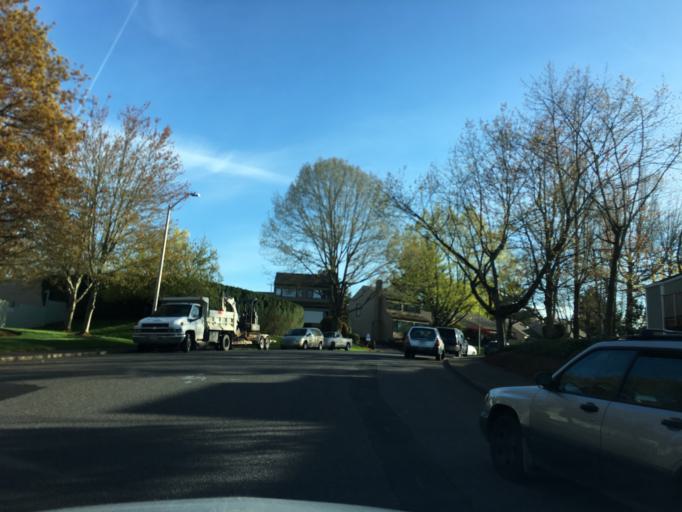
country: US
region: Oregon
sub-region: Multnomah County
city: Lents
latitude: 45.5537
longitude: -122.5328
